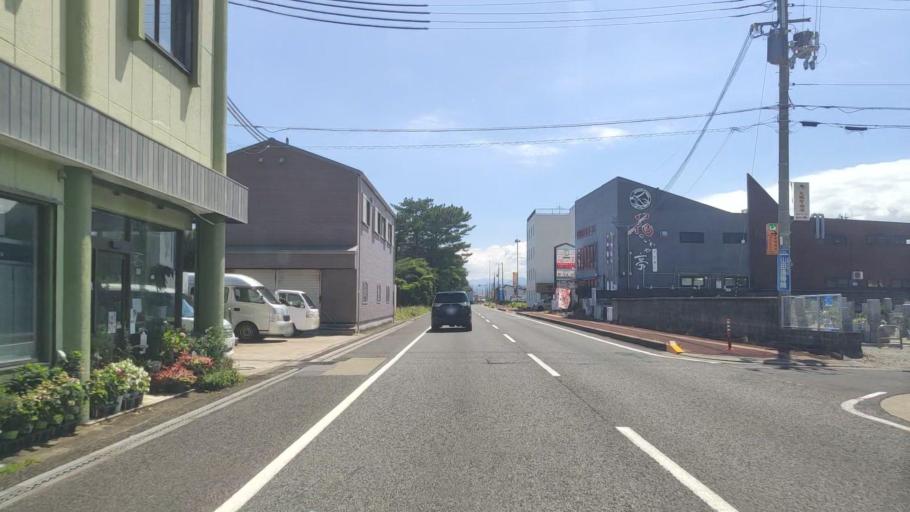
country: JP
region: Wakayama
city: Shingu
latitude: 33.8777
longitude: 136.0915
